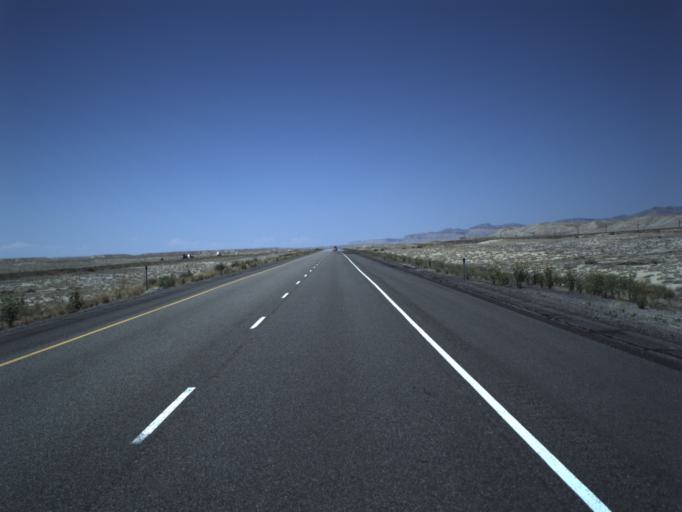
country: US
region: Utah
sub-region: Grand County
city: Moab
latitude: 38.9339
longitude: -109.4427
